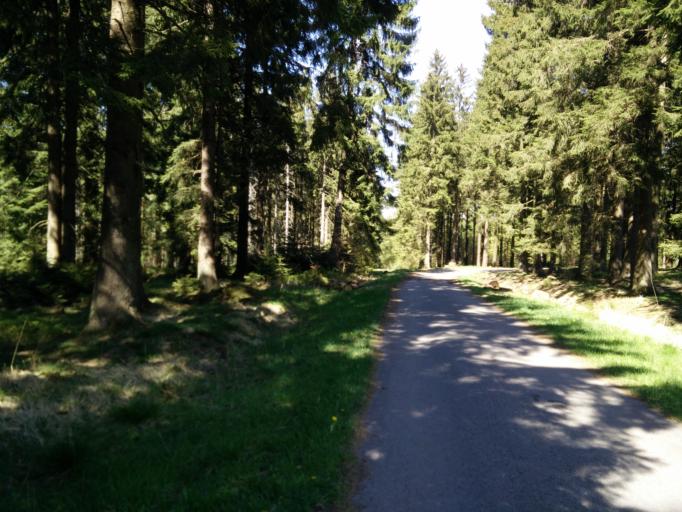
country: BE
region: Wallonia
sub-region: Province de Liege
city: Raeren
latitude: 50.5898
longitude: 6.1328
